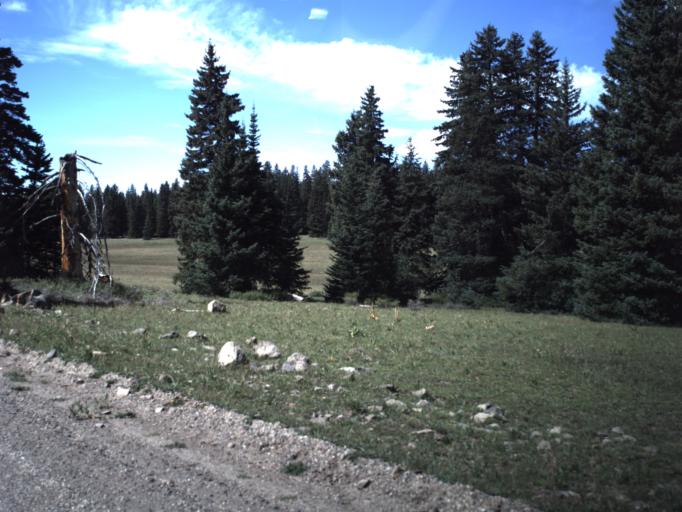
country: US
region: Utah
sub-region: Piute County
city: Junction
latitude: 38.2670
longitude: -112.3705
